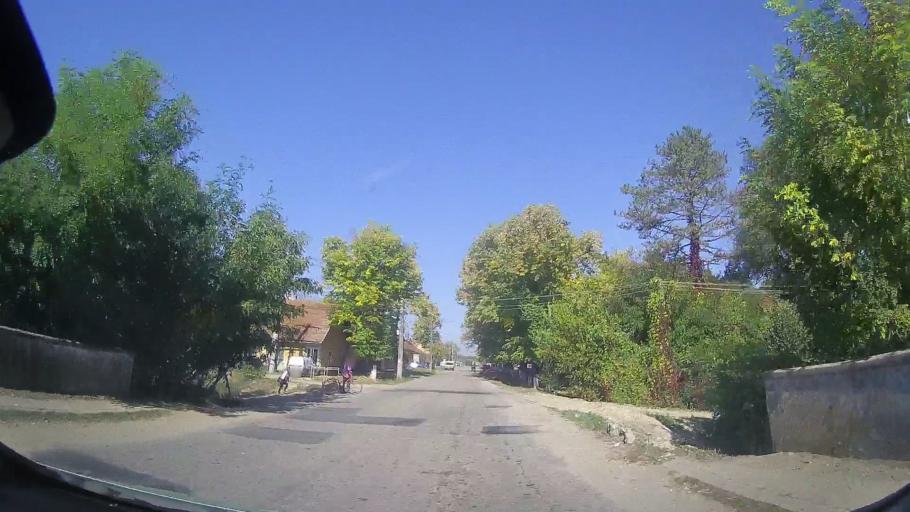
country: RO
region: Timis
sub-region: Comuna Balint
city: Balint
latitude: 45.8121
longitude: 21.8582
